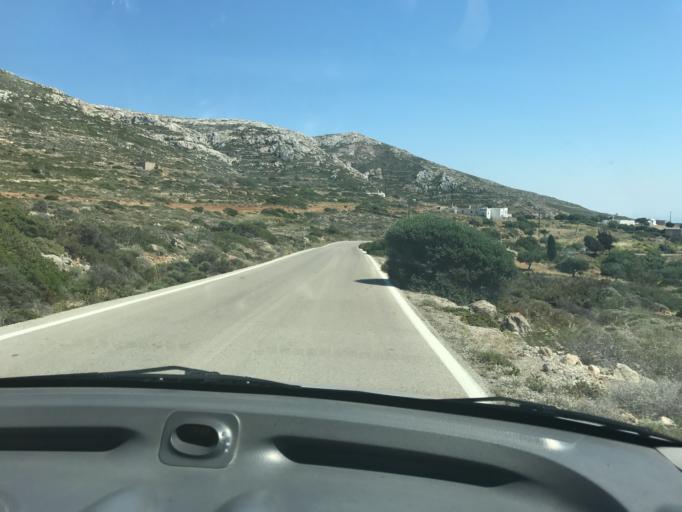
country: GR
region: South Aegean
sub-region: Nomos Dodekanisou
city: Karpathos
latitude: 35.4808
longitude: 27.1532
